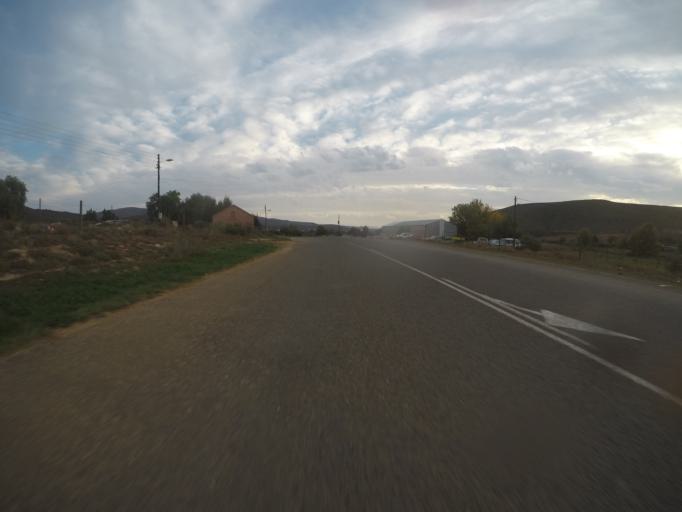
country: ZA
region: Western Cape
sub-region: Eden District Municipality
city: Knysna
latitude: -33.6447
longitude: 23.1375
